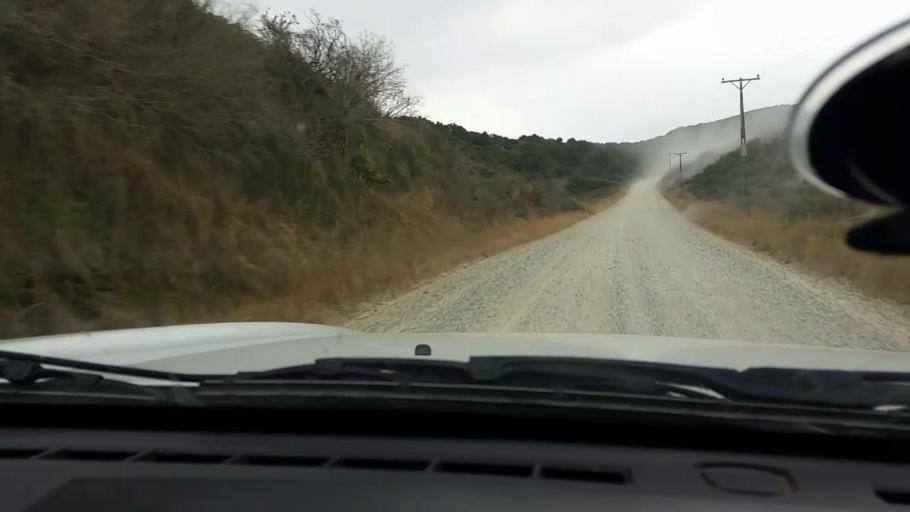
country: NZ
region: Otago
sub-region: Clutha District
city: Papatowai
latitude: -46.4678
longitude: 169.1297
